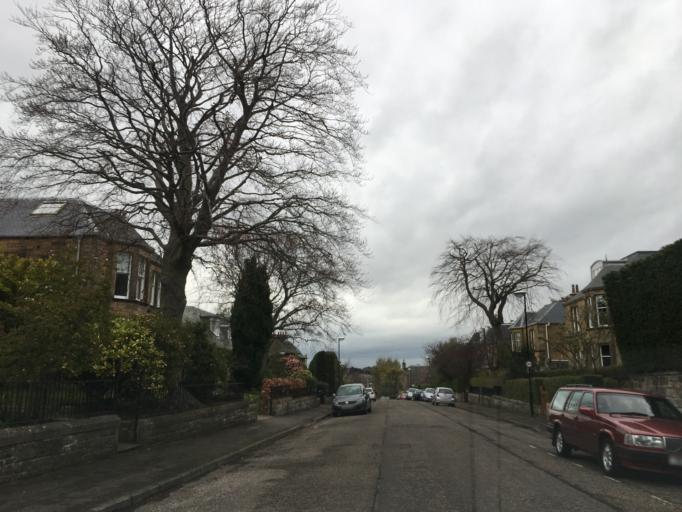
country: GB
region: Scotland
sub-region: Edinburgh
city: Edinburgh
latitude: 55.9207
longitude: -3.2081
